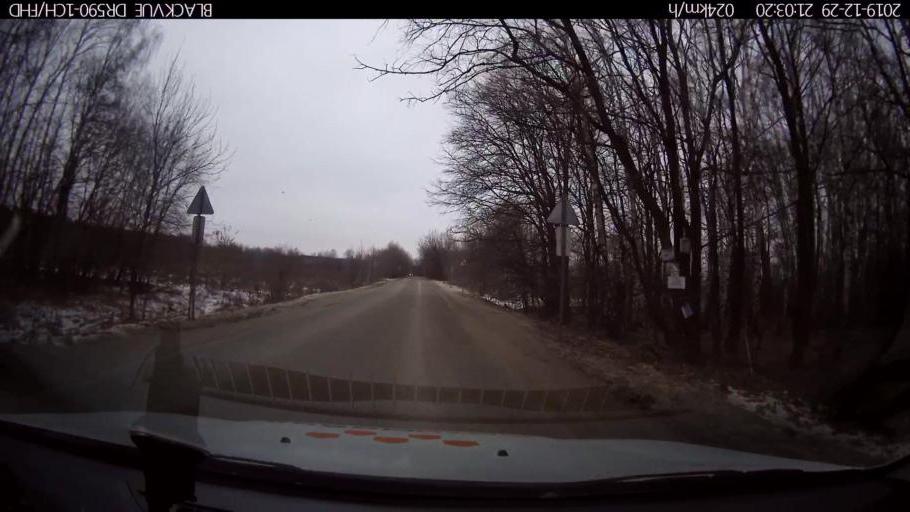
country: RU
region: Nizjnij Novgorod
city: Afonino
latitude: 56.1946
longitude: 44.0053
